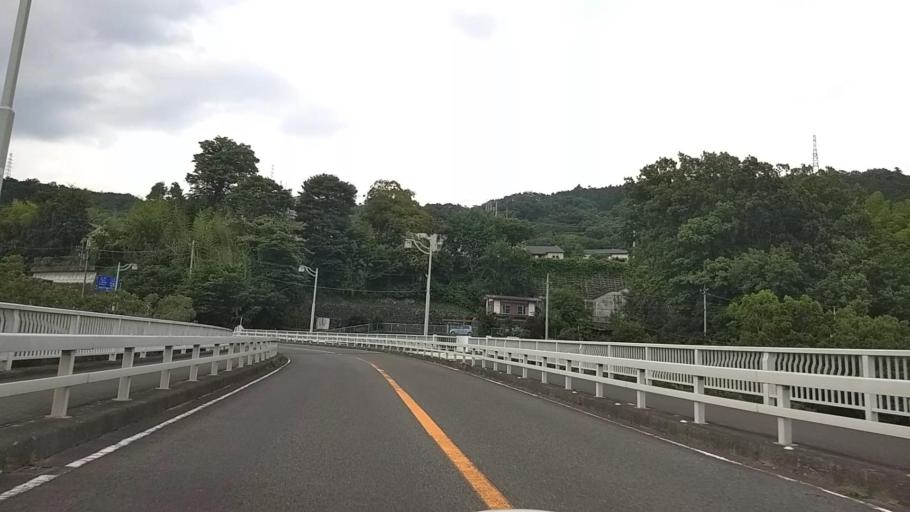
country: JP
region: Yamanashi
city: Uenohara
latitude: 35.6135
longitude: 139.1559
